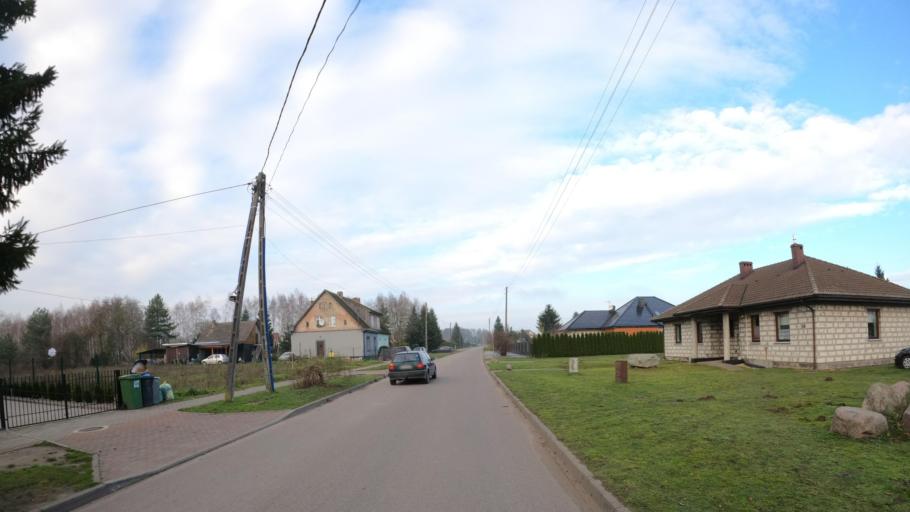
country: PL
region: West Pomeranian Voivodeship
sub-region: Powiat goleniowski
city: Maszewo
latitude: 53.5063
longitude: 15.0558
